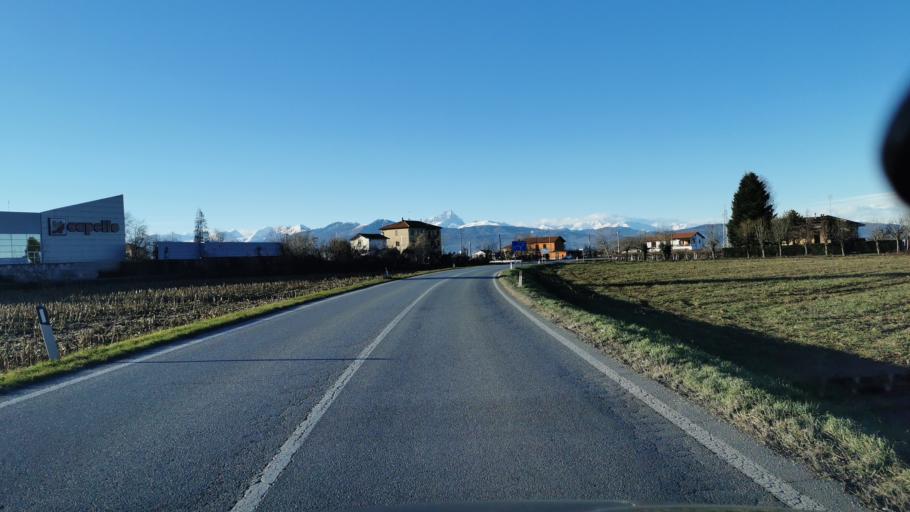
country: IT
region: Piedmont
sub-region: Provincia di Cuneo
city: Roata Rossi
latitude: 44.4267
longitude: 7.5468
